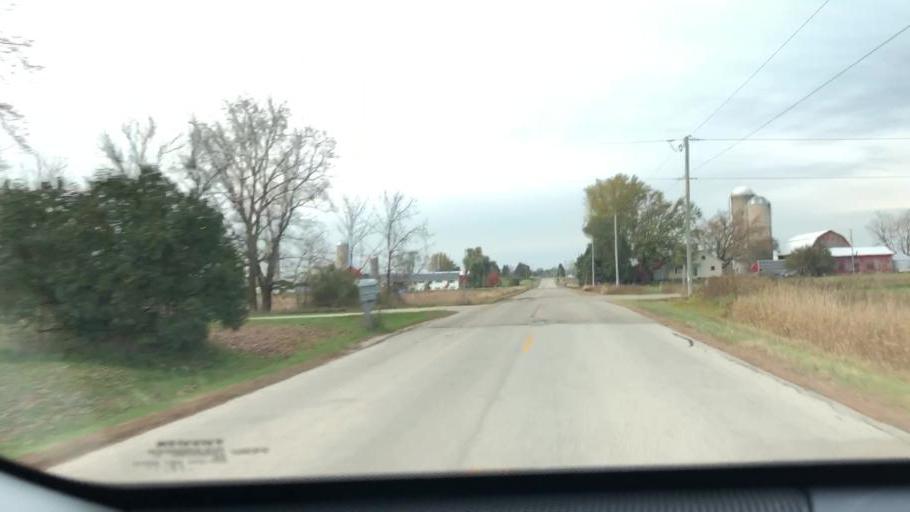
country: US
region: Wisconsin
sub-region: Outagamie County
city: Seymour
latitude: 44.4576
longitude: -88.3498
